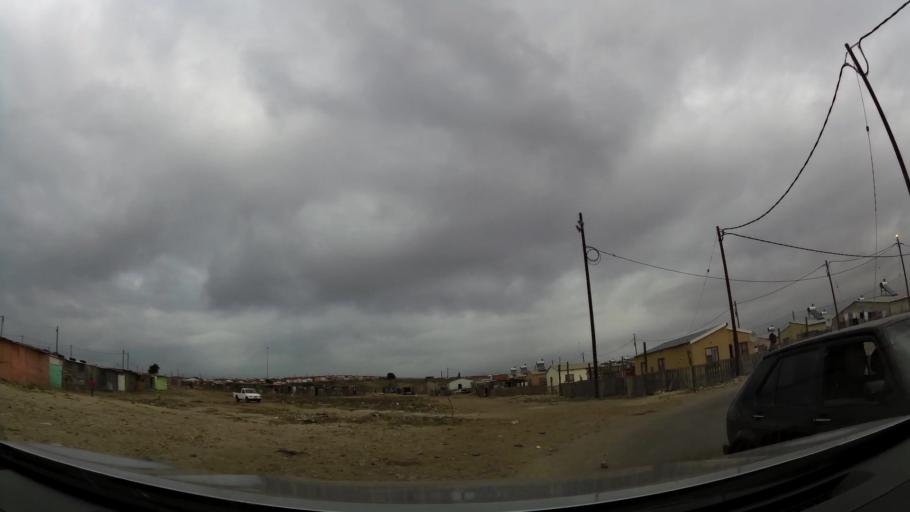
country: ZA
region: Eastern Cape
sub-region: Nelson Mandela Bay Metropolitan Municipality
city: Port Elizabeth
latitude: -33.8880
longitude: 25.6049
